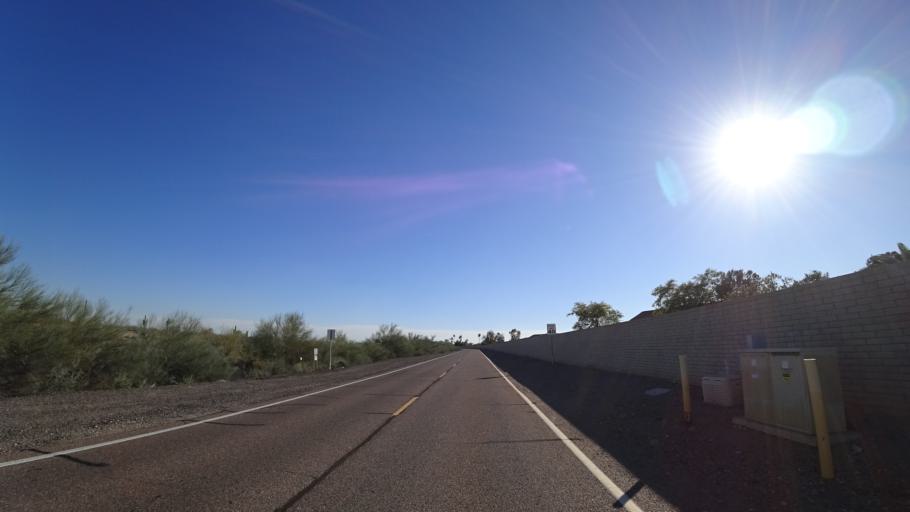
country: US
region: Arizona
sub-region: Maricopa County
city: Sun City West
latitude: 33.6778
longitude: -112.3257
